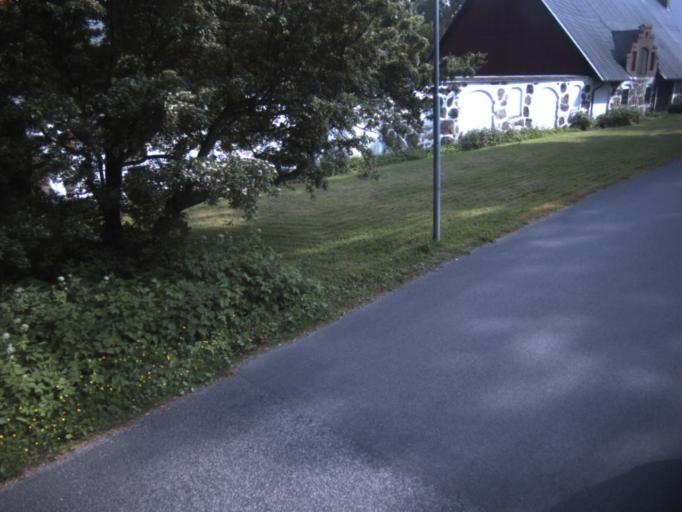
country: SE
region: Skane
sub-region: Helsingborg
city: Helsingborg
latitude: 56.0687
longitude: 12.6816
